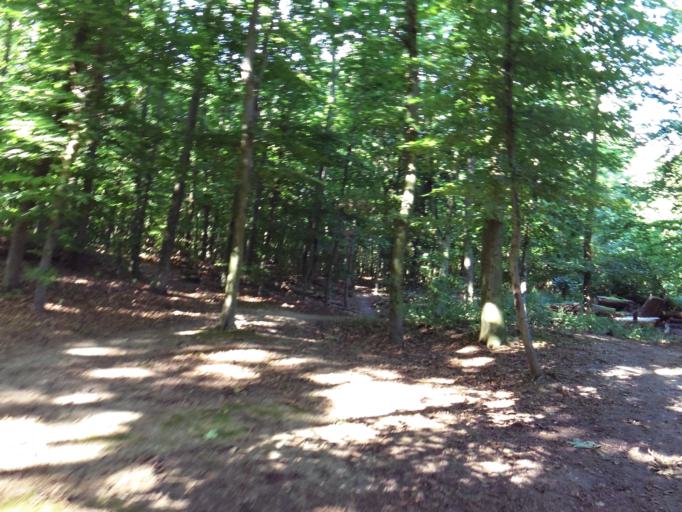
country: DE
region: North Rhine-Westphalia
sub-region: Regierungsbezirk Koln
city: Alsdorf
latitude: 50.8554
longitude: 6.1877
